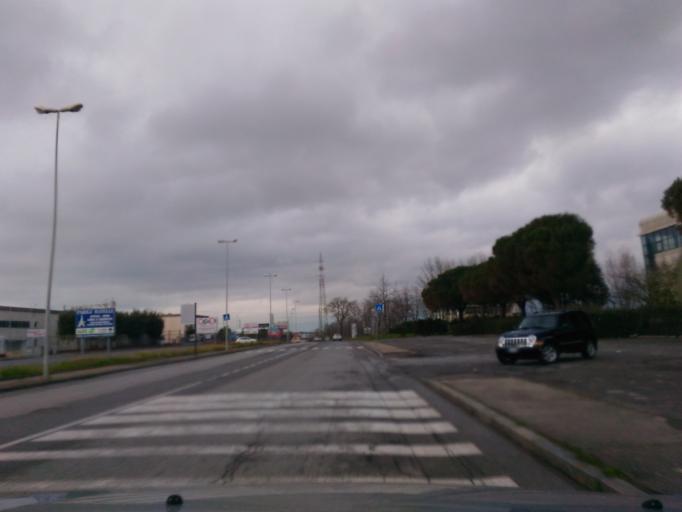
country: IT
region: Tuscany
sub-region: Provincia di Livorno
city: Livorno
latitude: 43.5707
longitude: 10.3391
